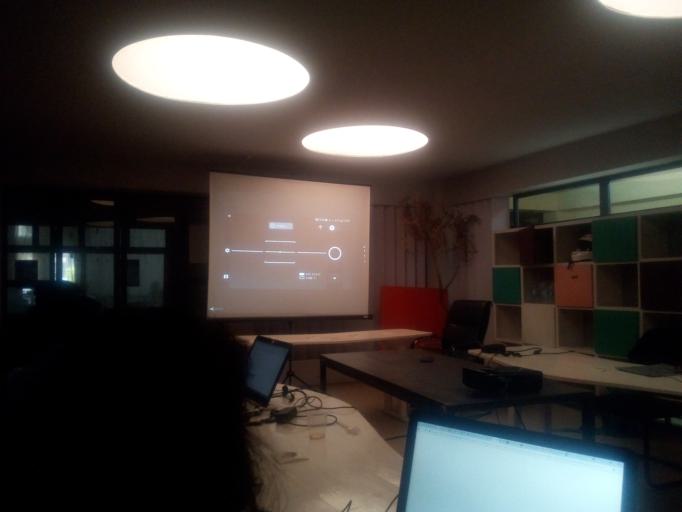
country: MG
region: Analamanga
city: Antananarivo
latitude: -18.9313
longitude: 47.5282
